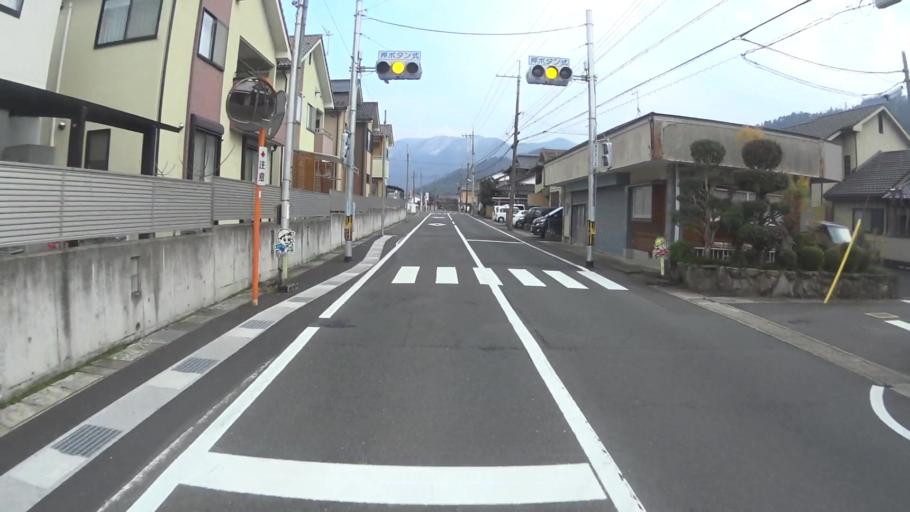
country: JP
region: Kyoto
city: Maizuru
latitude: 35.4509
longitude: 135.4031
